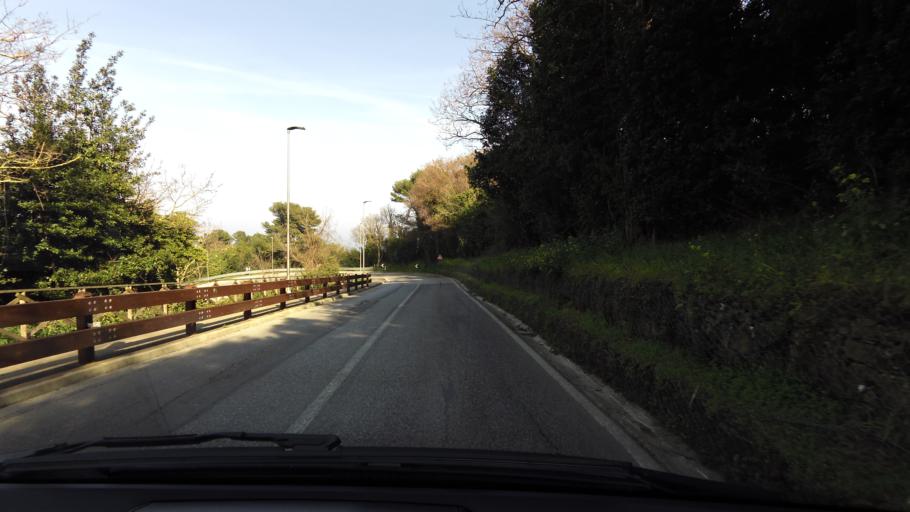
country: IT
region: The Marches
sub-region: Provincia di Ancona
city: Numana
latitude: 43.5072
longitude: 13.6192
